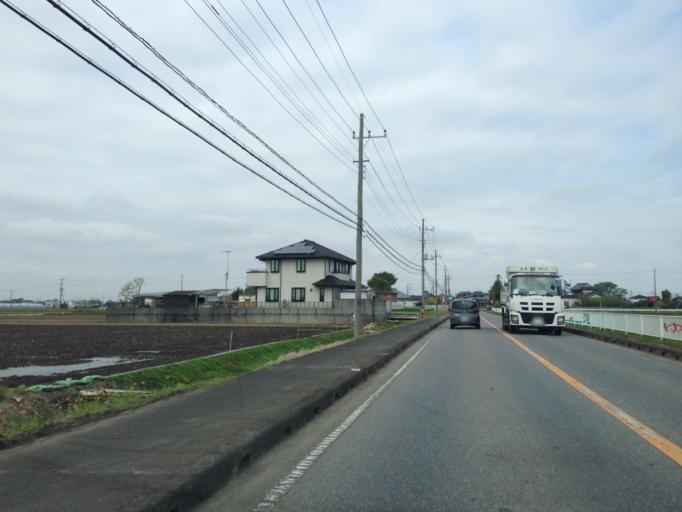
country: JP
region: Ibaraki
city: Ishige
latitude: 36.1520
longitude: 139.9879
